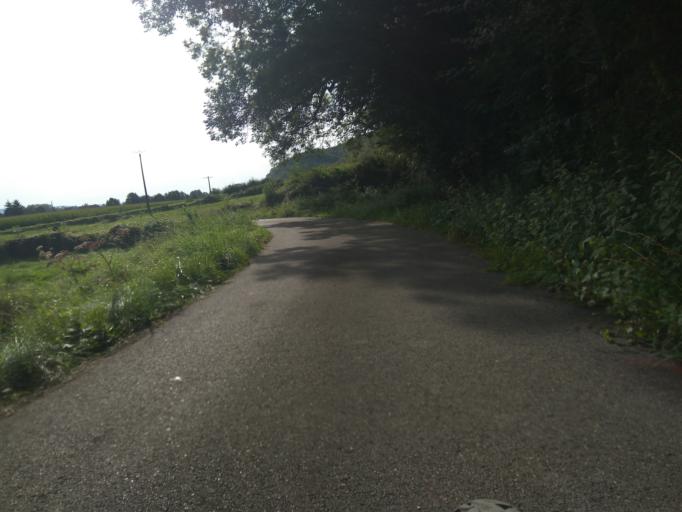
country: FR
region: Aquitaine
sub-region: Departement des Pyrenees-Atlantiques
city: Mazeres-Lezons
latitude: 43.2664
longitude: -0.3450
